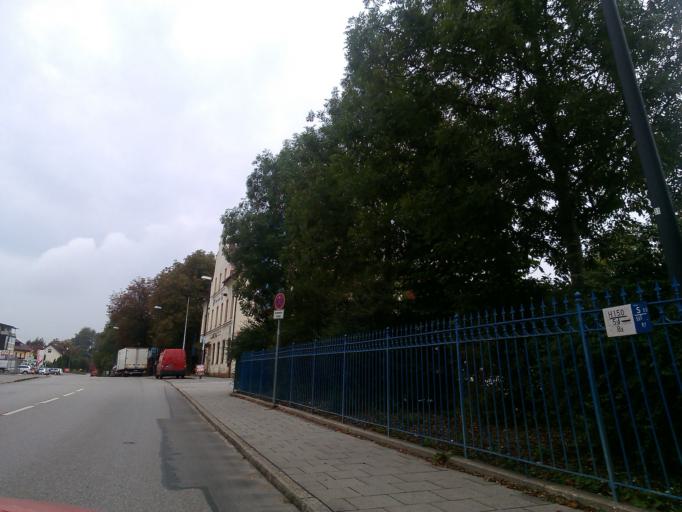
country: DE
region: Bavaria
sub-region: Upper Bavaria
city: Olching
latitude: 48.2051
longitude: 11.3254
